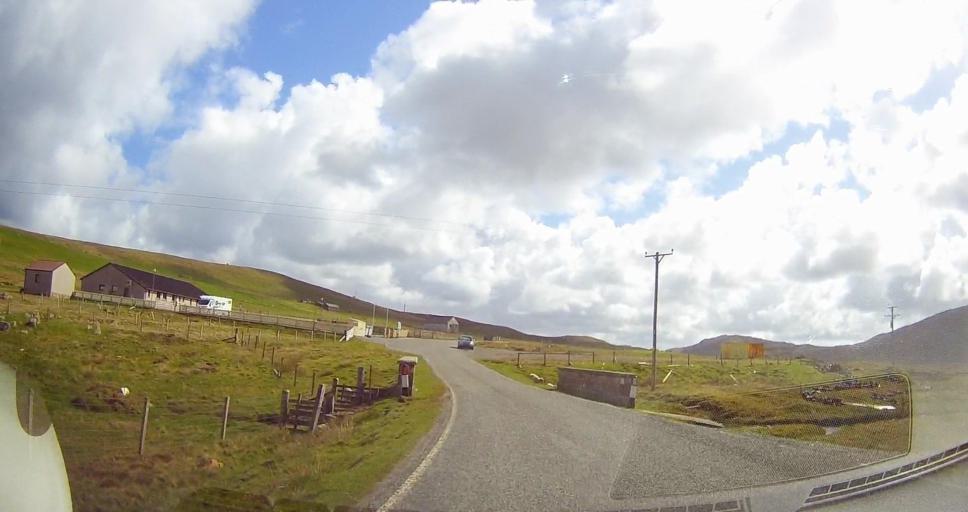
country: GB
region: Scotland
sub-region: Shetland Islands
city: Lerwick
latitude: 60.5720
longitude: -1.3326
